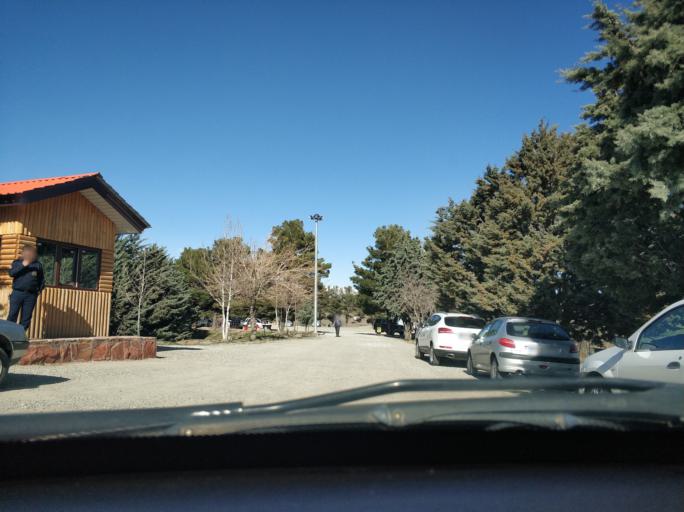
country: IR
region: Tehran
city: Tajrish
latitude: 35.7995
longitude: 51.5665
